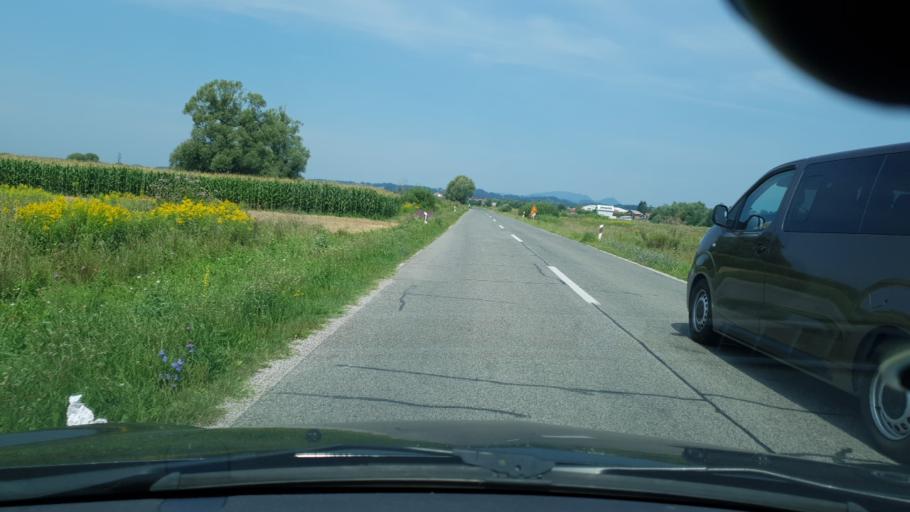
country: HR
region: Krapinsko-Zagorska
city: Marija Bistrica
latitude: 46.0378
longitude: 16.0869
